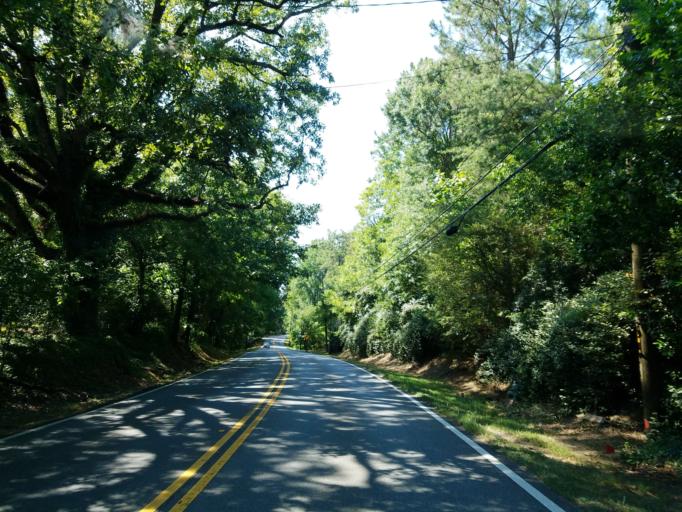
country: US
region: Georgia
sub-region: Fulton County
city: Milton
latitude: 34.1037
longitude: -84.3397
